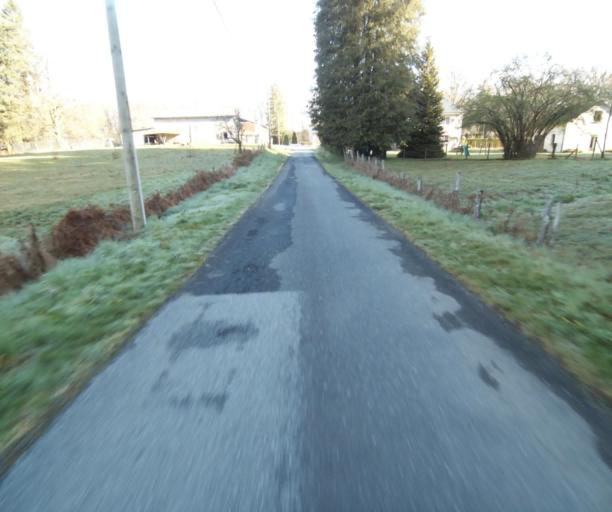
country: FR
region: Limousin
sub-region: Departement de la Correze
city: Correze
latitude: 45.2856
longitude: 1.8656
